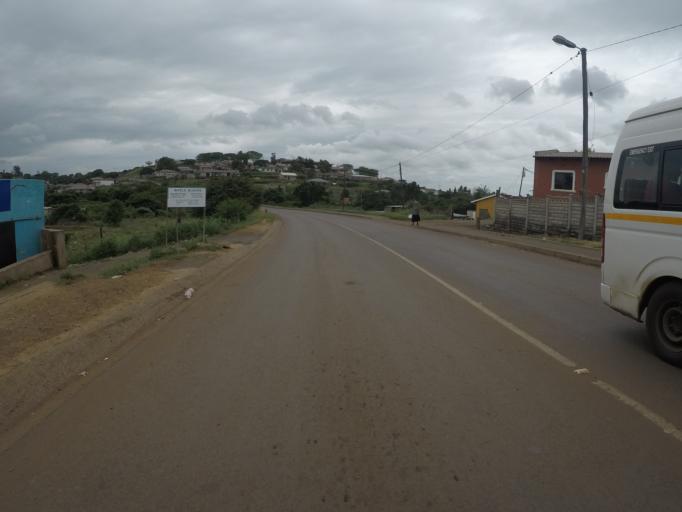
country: ZA
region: KwaZulu-Natal
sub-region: uThungulu District Municipality
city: Empangeni
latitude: -28.7825
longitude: 31.8618
